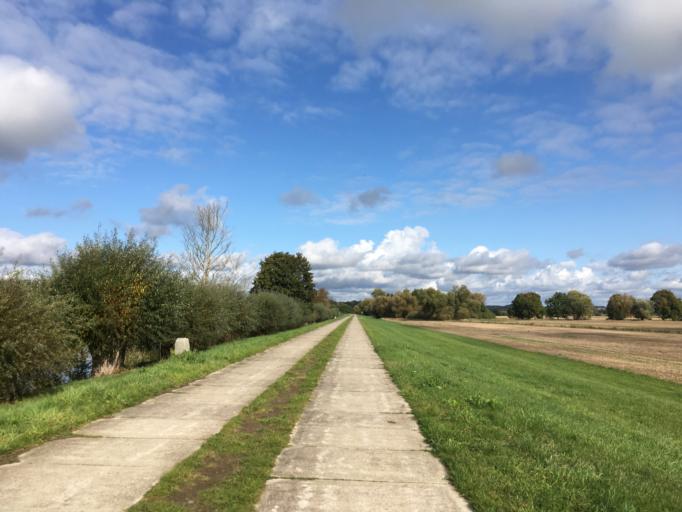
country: DE
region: Brandenburg
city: Schoneberg
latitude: 52.9627
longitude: 14.1092
